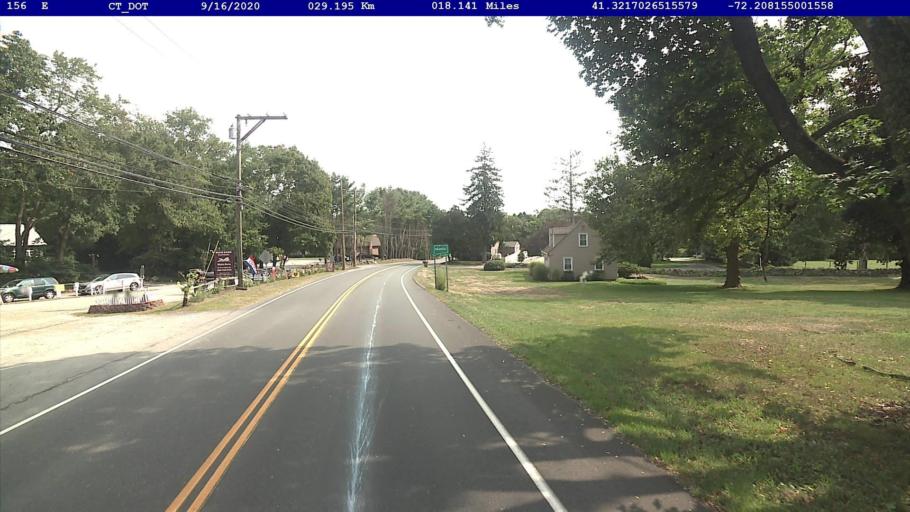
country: US
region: Connecticut
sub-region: New London County
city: Niantic
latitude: 41.3217
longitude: -72.2082
